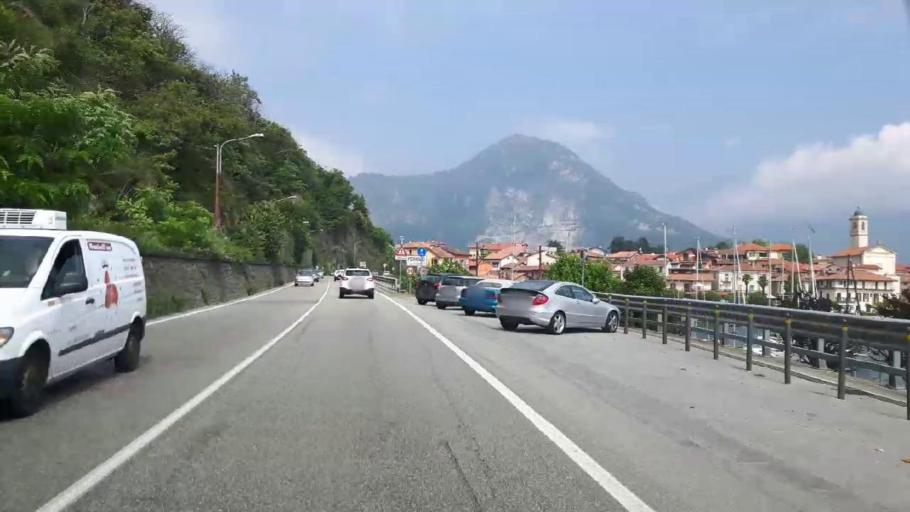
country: IT
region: Piedmont
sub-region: Provincia Verbano-Cusio-Ossola
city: Baveno
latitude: 45.9274
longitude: 8.4824
